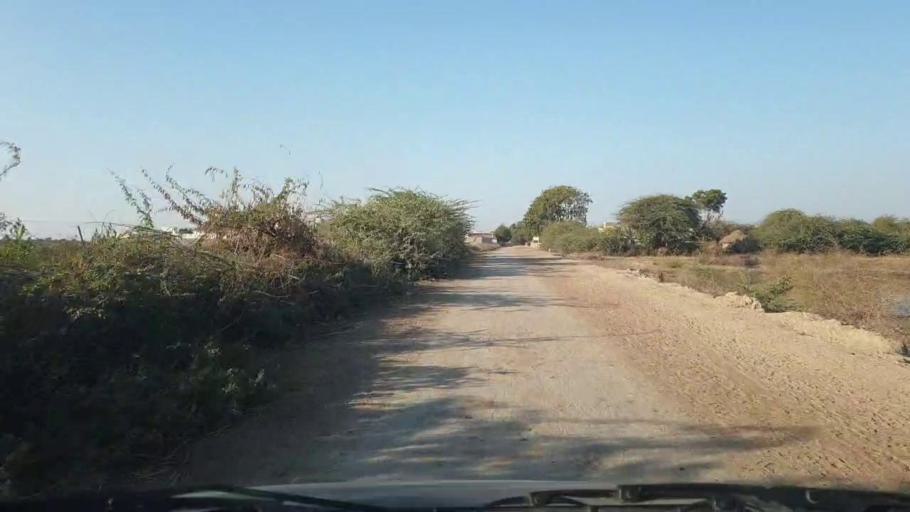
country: PK
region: Sindh
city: Samaro
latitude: 25.3413
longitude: 69.3050
